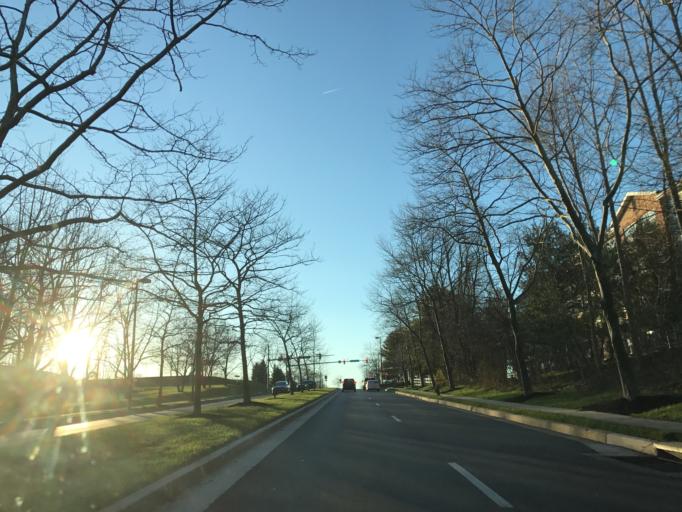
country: US
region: Maryland
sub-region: Baltimore County
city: Owings Mills
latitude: 39.4039
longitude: -76.8094
